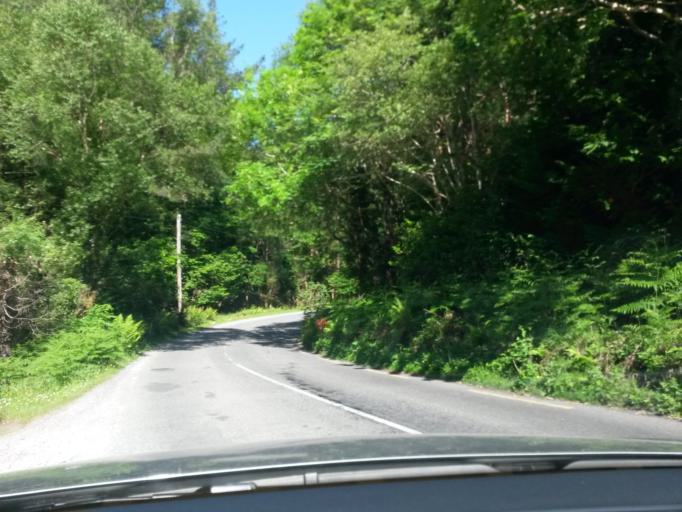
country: IE
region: Munster
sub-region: Ciarrai
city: Kenmare
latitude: 51.7598
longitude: -9.8037
